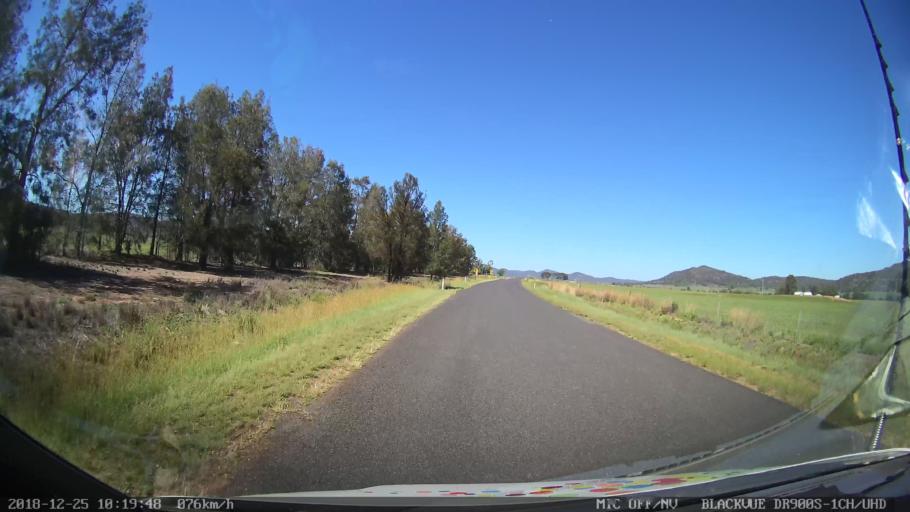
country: AU
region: New South Wales
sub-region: Muswellbrook
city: Denman
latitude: -32.3540
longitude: 150.5556
